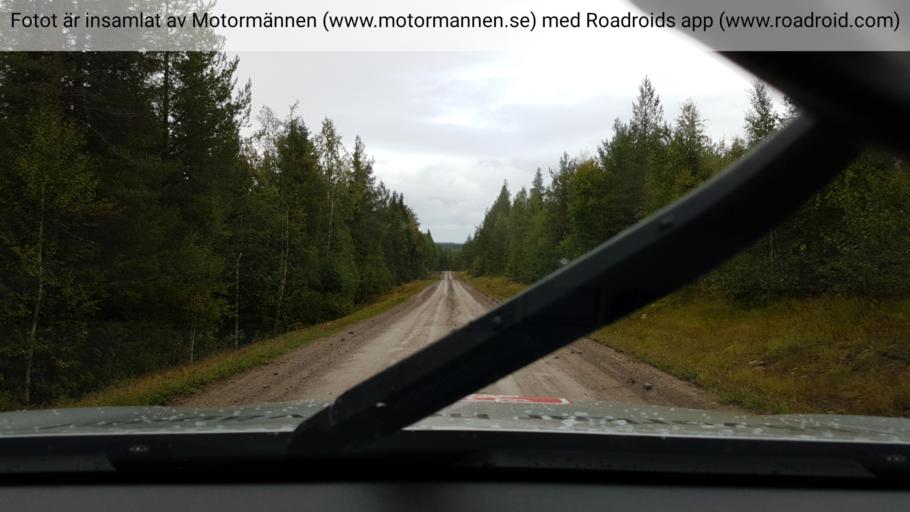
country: SE
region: Vaesterbotten
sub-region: Norsjo Kommun
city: Norsjoe
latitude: 65.2267
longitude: 19.8512
